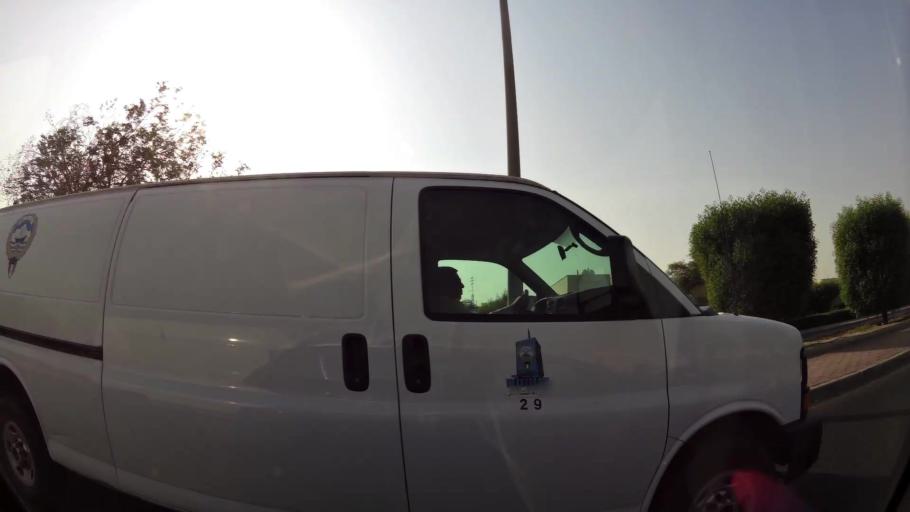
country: KW
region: Mubarak al Kabir
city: Mubarak al Kabir
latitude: 29.1786
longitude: 48.0754
